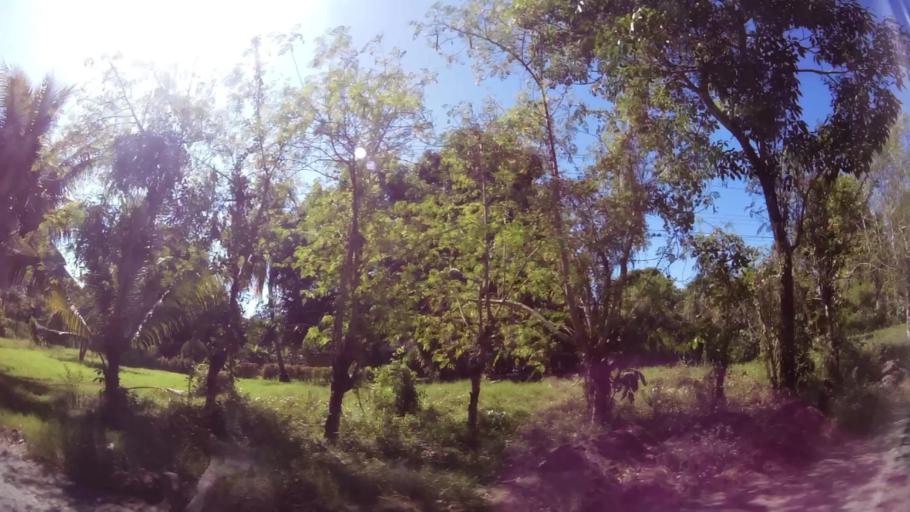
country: GT
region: Escuintla
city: Iztapa
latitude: 13.9137
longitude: -90.5419
